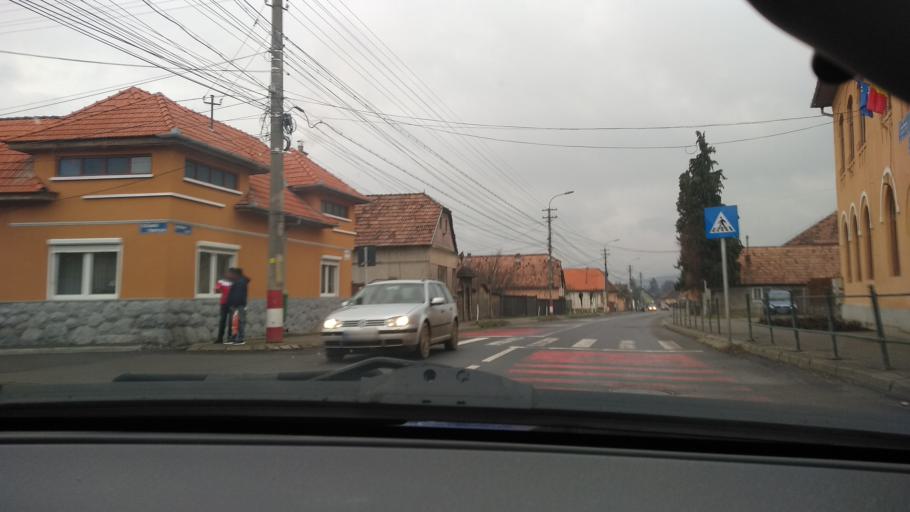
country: RO
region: Mures
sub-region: Oras Sovata
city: Sovata
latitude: 46.5863
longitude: 25.0647
